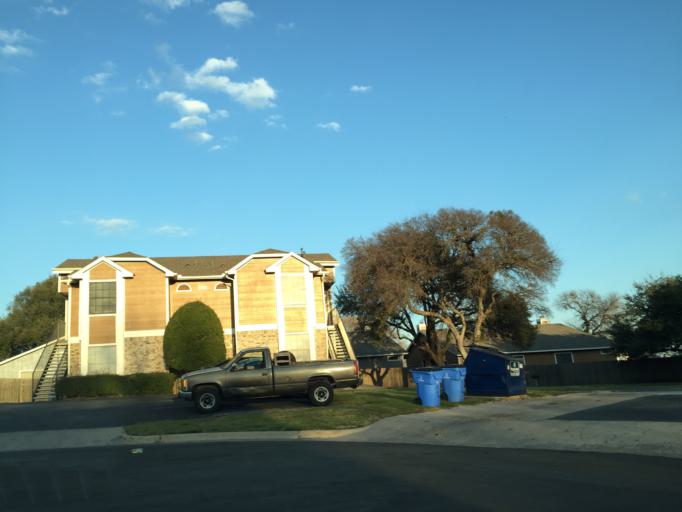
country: US
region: Texas
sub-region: Williamson County
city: Jollyville
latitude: 30.4384
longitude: -97.7469
